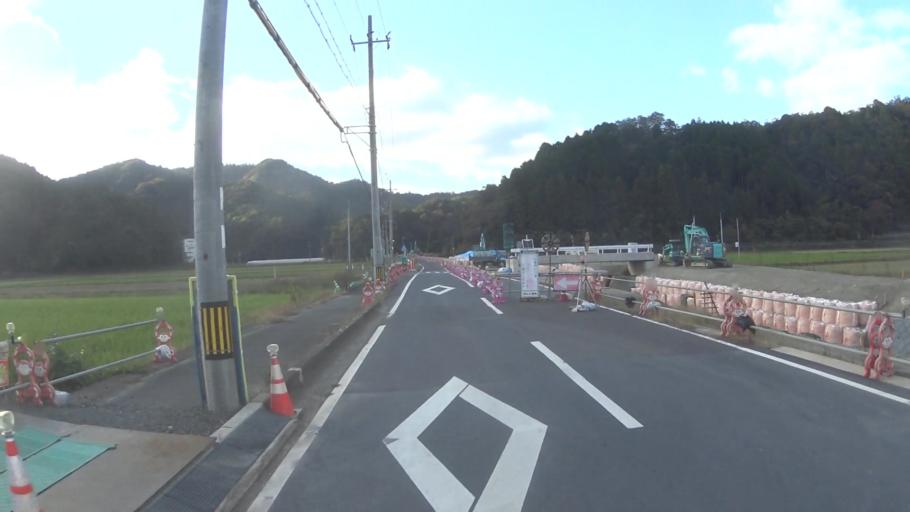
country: JP
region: Kyoto
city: Maizuru
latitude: 35.4507
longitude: 135.2629
